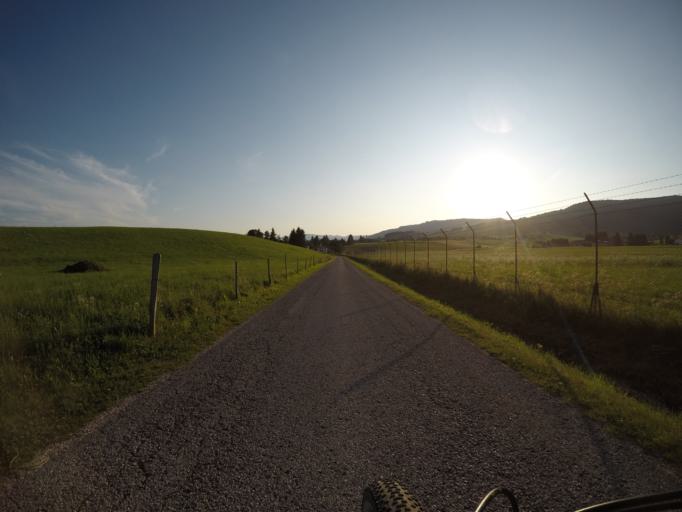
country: IT
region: Veneto
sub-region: Provincia di Vicenza
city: Asiago
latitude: 45.8837
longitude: 11.5143
